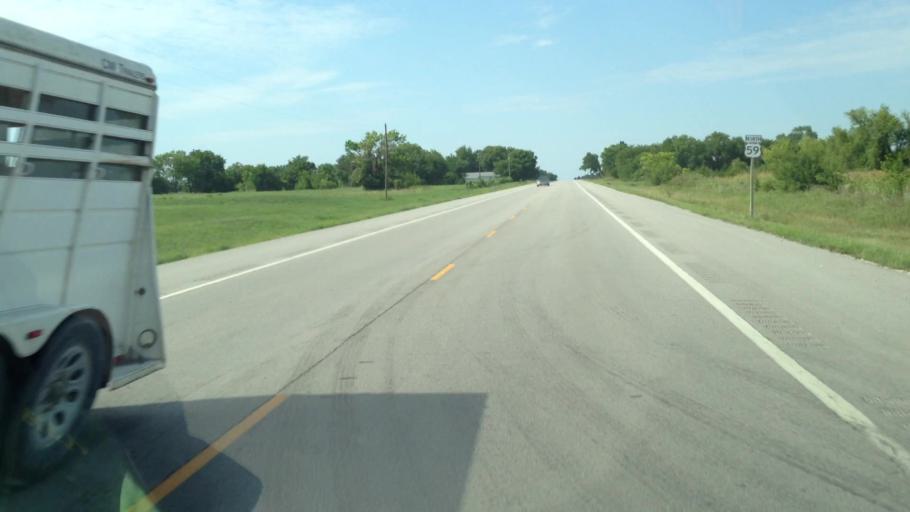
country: US
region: Kansas
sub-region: Labette County
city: Altamont
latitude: 37.2520
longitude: -95.2671
